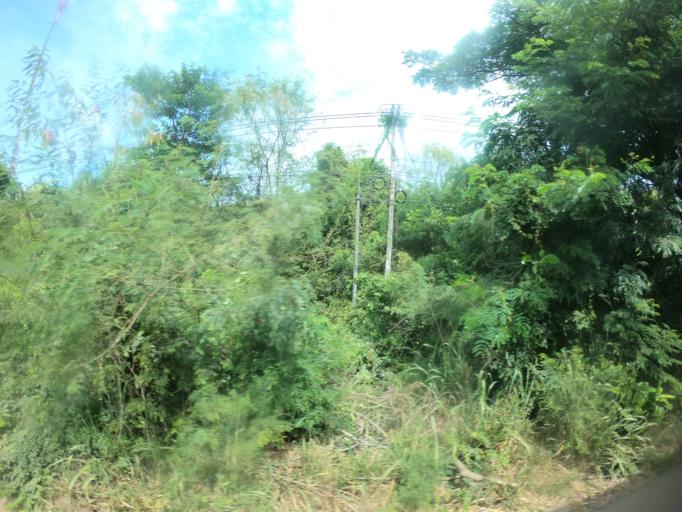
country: TH
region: Maha Sarakham
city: Chiang Yuen
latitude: 16.3436
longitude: 103.1404
